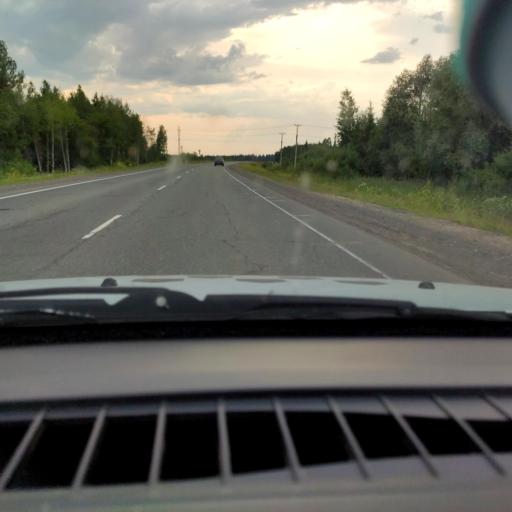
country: RU
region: Udmurtiya
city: Debesy
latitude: 57.6043
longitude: 53.4535
